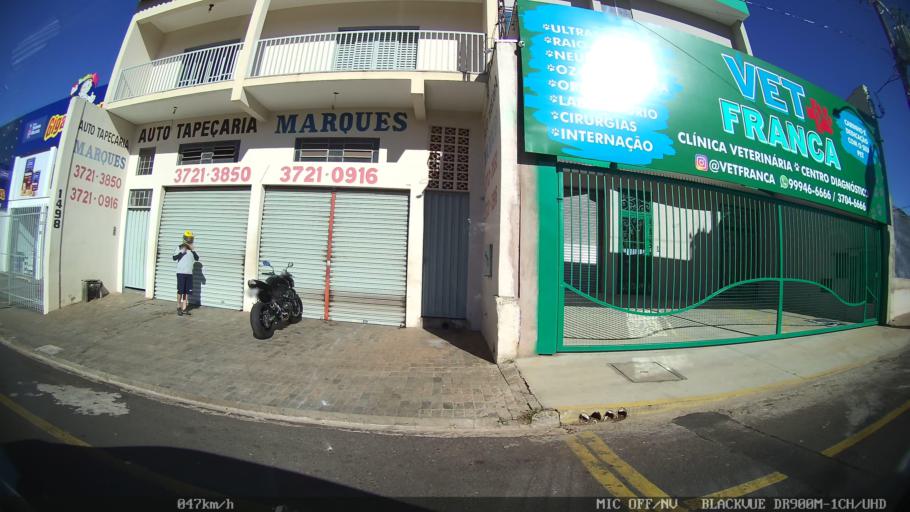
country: BR
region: Sao Paulo
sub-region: Franca
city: Franca
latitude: -20.5489
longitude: -47.4095
